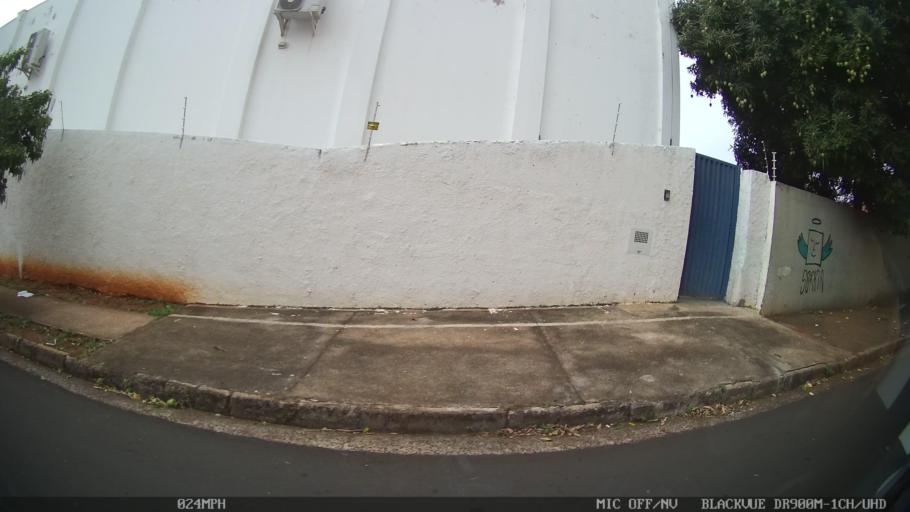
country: BR
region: Sao Paulo
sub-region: Sao Jose Do Rio Preto
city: Sao Jose do Rio Preto
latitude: -20.8305
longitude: -49.3918
